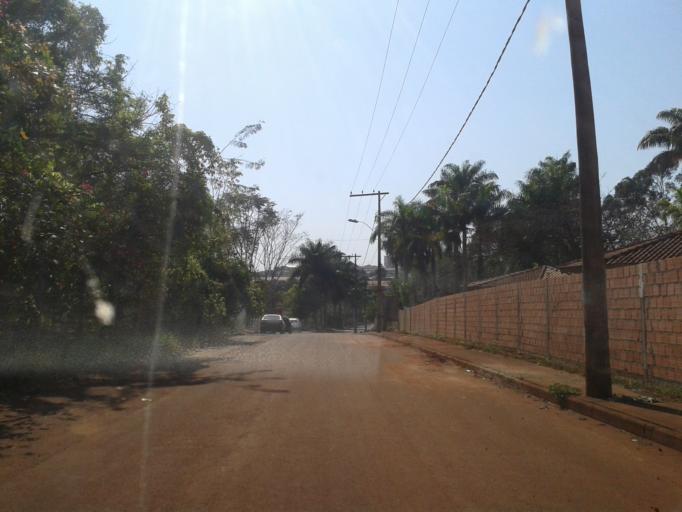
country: BR
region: Minas Gerais
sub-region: Ituiutaba
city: Ituiutaba
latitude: -18.9649
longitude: -49.4756
